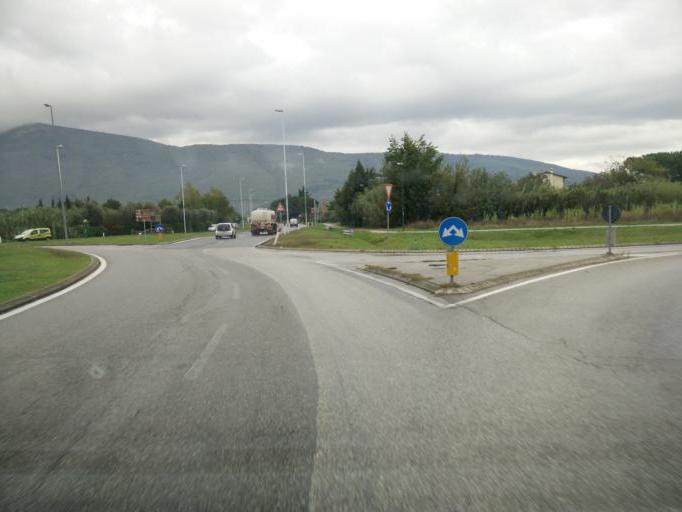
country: IT
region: Tuscany
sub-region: Provincia di Prato
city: Prato
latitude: 43.9023
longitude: 11.0919
